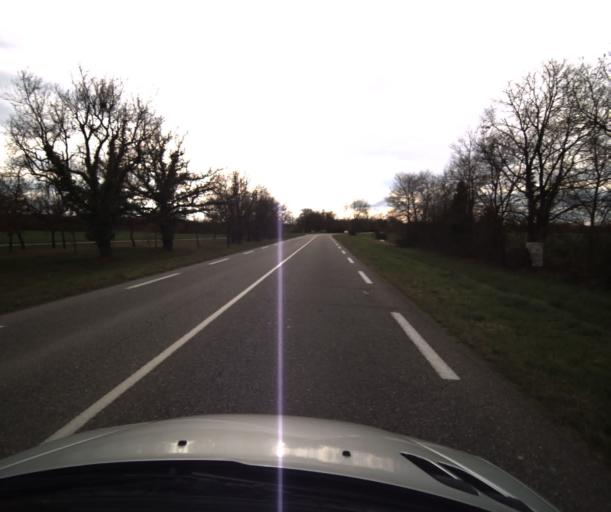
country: FR
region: Midi-Pyrenees
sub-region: Departement du Tarn-et-Garonne
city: Saint-Etienne-de-Tulmont
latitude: 44.0325
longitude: 1.4098
